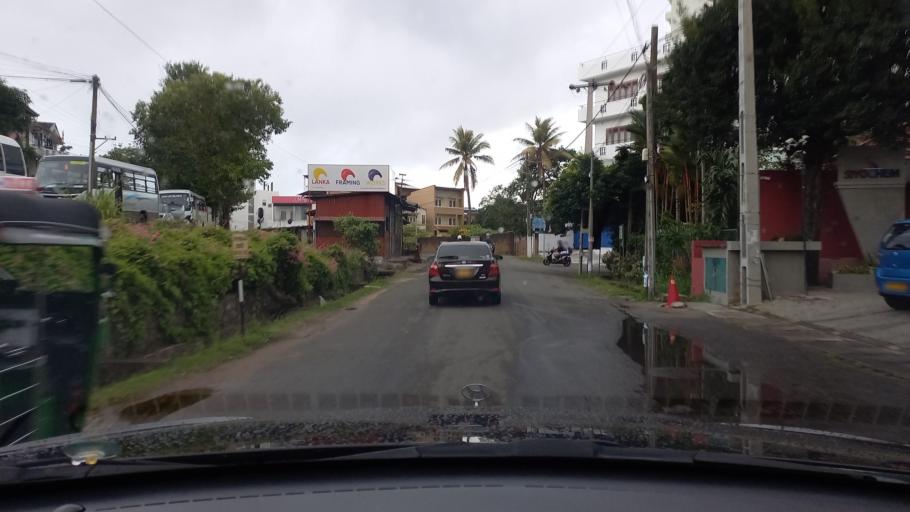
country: LK
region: Western
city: Sri Jayewardenepura Kotte
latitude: 6.8731
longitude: 79.8888
